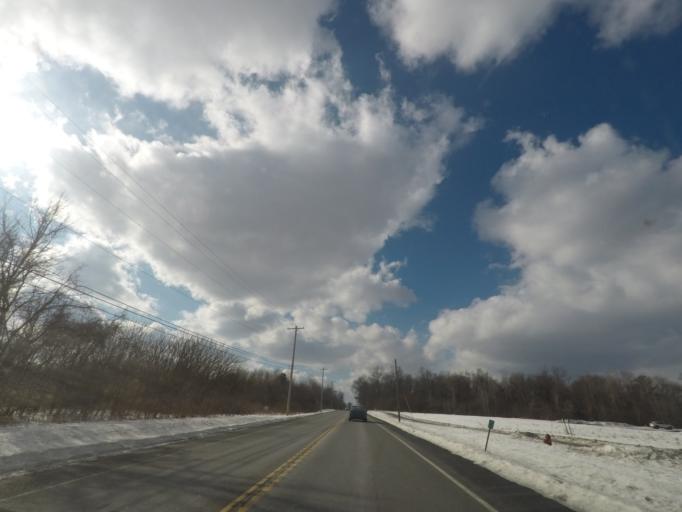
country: US
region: New York
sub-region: Schenectady County
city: East Glenville
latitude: 42.8681
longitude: -73.8695
